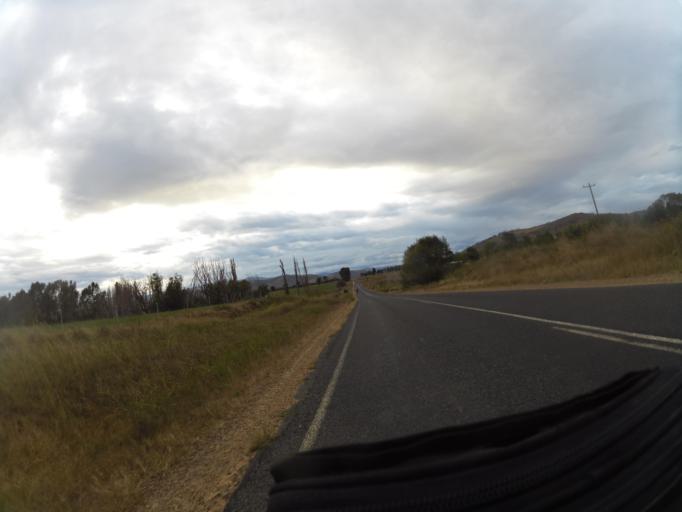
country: AU
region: New South Wales
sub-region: Greater Hume Shire
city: Holbrook
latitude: -36.0657
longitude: 147.9519
